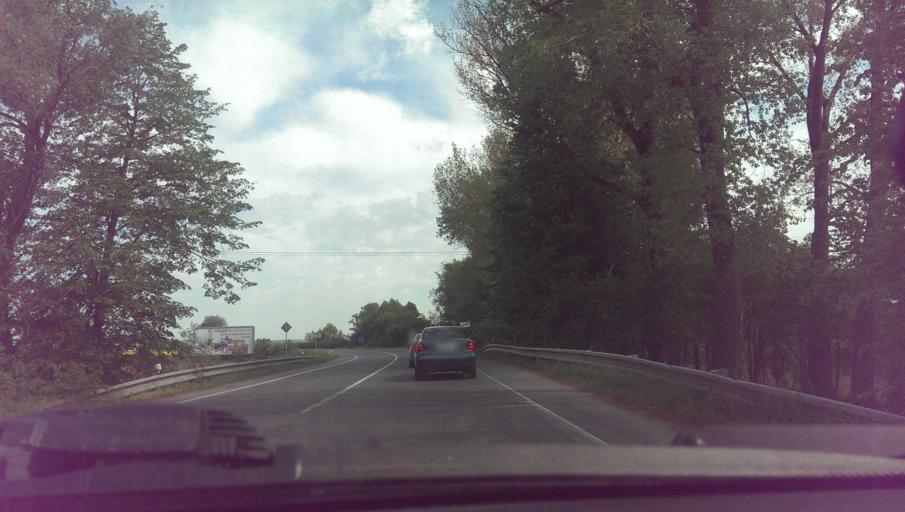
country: CZ
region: Zlin
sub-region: Okres Uherske Hradiste
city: Stare Mesto
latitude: 49.0869
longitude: 17.4490
